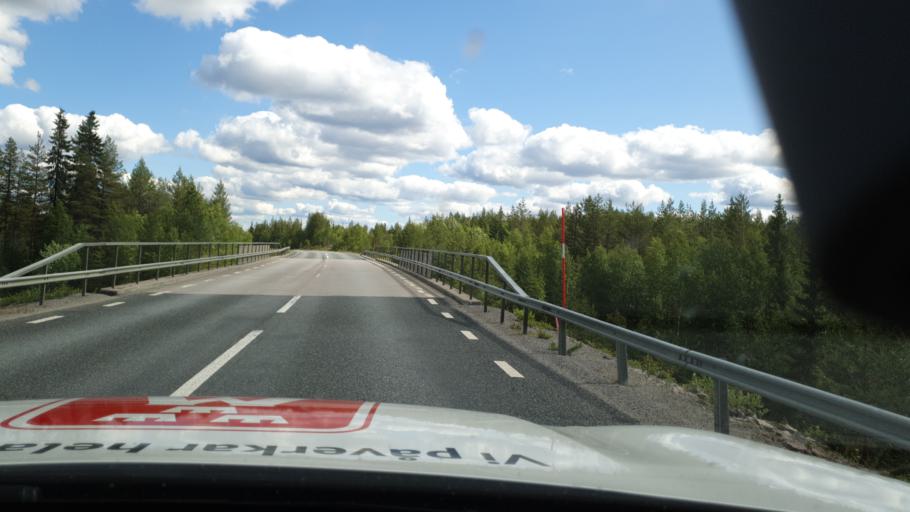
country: SE
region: Vaesterbotten
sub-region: Sorsele Kommun
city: Sorsele
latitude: 65.5584
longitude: 17.9192
